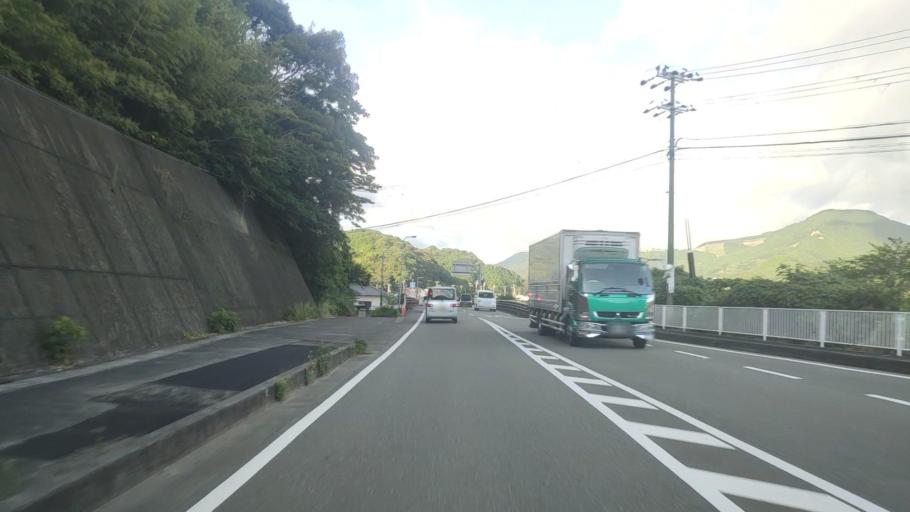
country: JP
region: Wakayama
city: Tanabe
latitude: 33.7146
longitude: 135.4562
